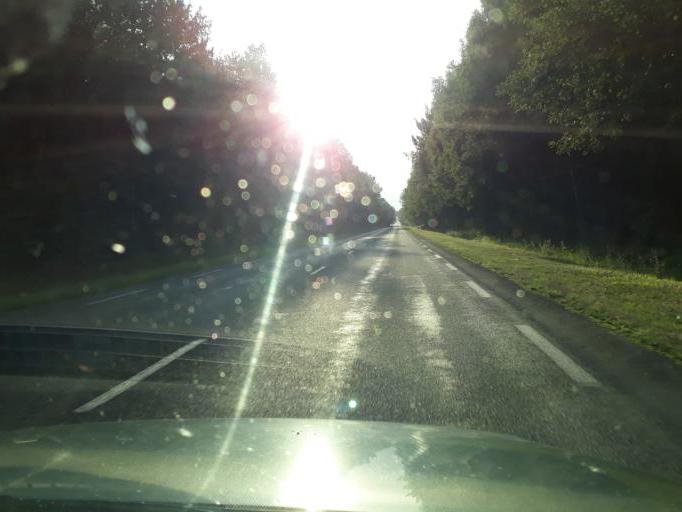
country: FR
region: Pays de la Loire
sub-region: Departement de la Sarthe
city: Le Breil-sur-Merize
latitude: 47.9962
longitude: 0.4452
